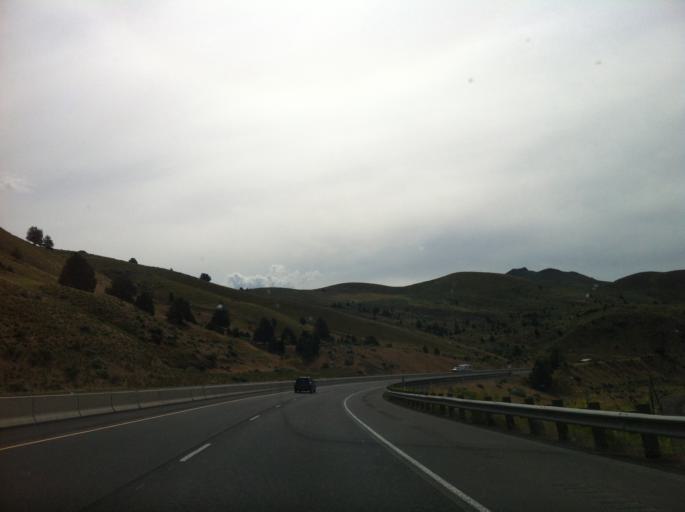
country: US
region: Idaho
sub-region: Washington County
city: Weiser
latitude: 44.5195
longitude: -117.3789
